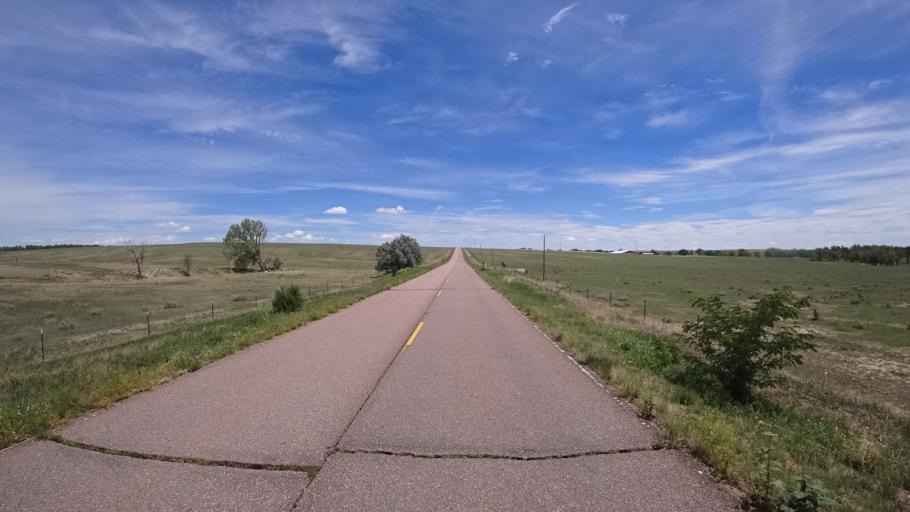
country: US
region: Colorado
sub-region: El Paso County
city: Fountain
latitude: 38.6940
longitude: -104.6034
